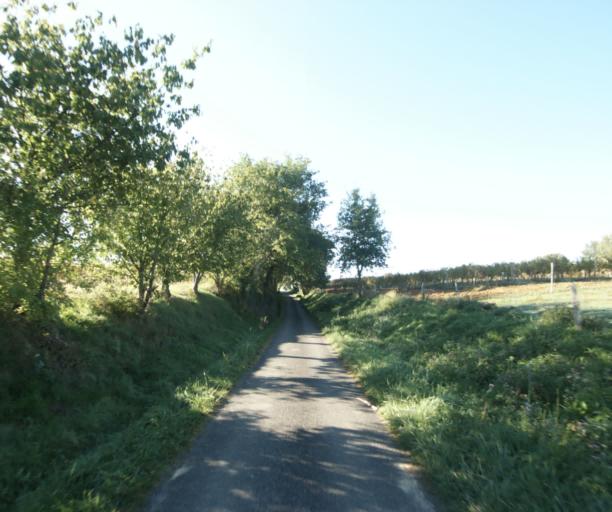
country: FR
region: Midi-Pyrenees
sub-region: Departement du Gers
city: Gondrin
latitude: 43.8446
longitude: 0.2329
